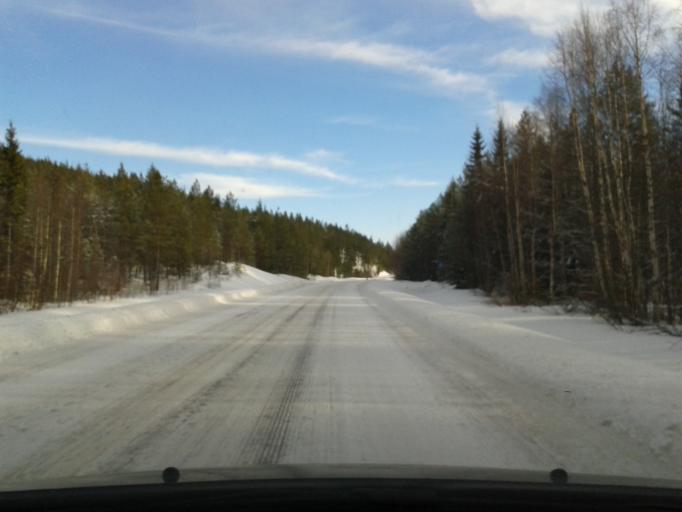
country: SE
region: Vaesterbotten
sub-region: Asele Kommun
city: Asele
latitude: 64.3205
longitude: 17.1136
